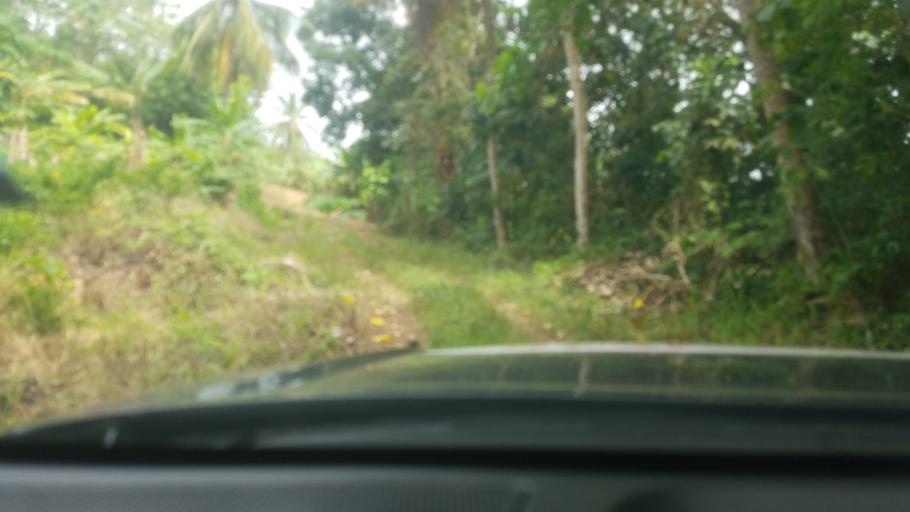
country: LC
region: Micoud Quarter
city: Micoud
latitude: 13.8058
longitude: -60.9353
